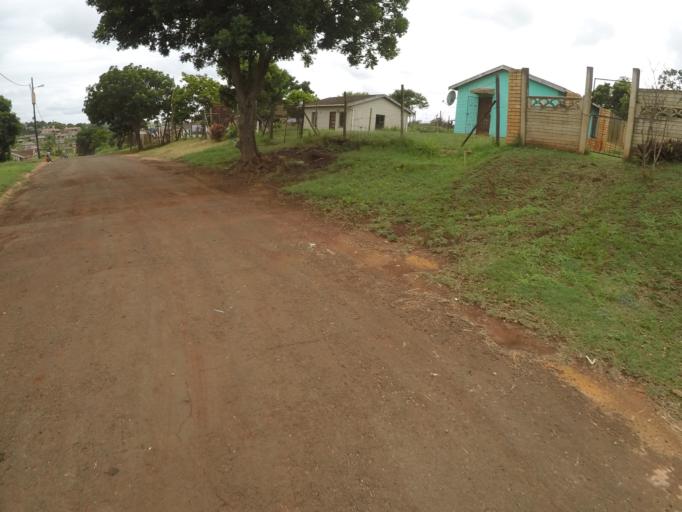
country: ZA
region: KwaZulu-Natal
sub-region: uThungulu District Municipality
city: Empangeni
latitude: -28.7806
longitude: 31.8565
